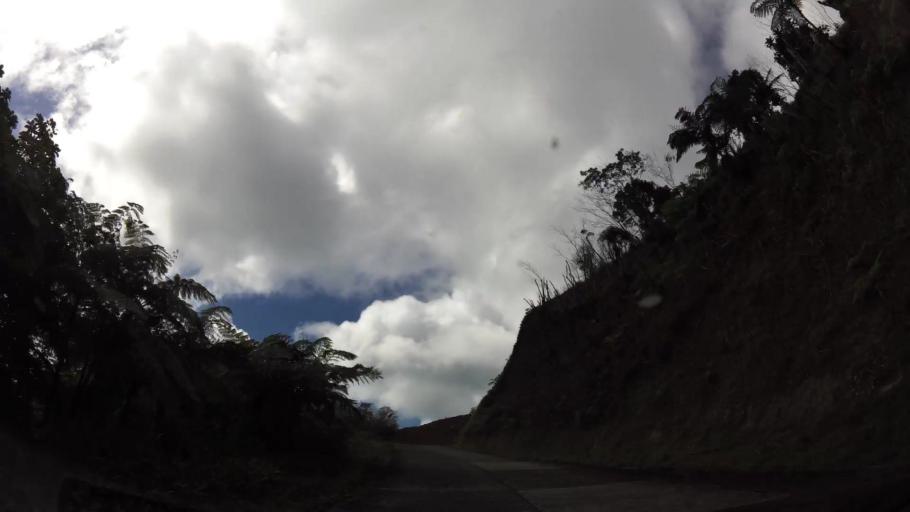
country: DM
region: Saint John
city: Portsmouth
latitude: 15.6143
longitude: -61.4465
